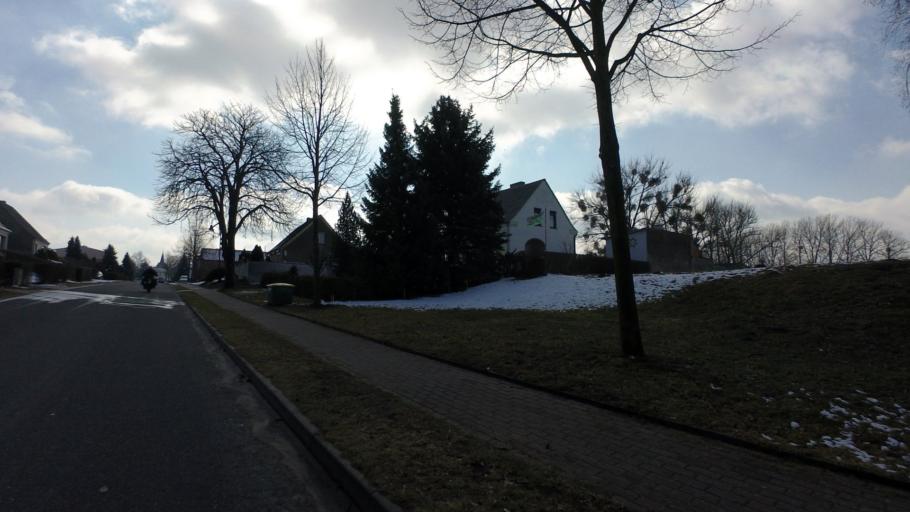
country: DE
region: Brandenburg
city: Werneuchen
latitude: 52.6842
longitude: 13.7319
